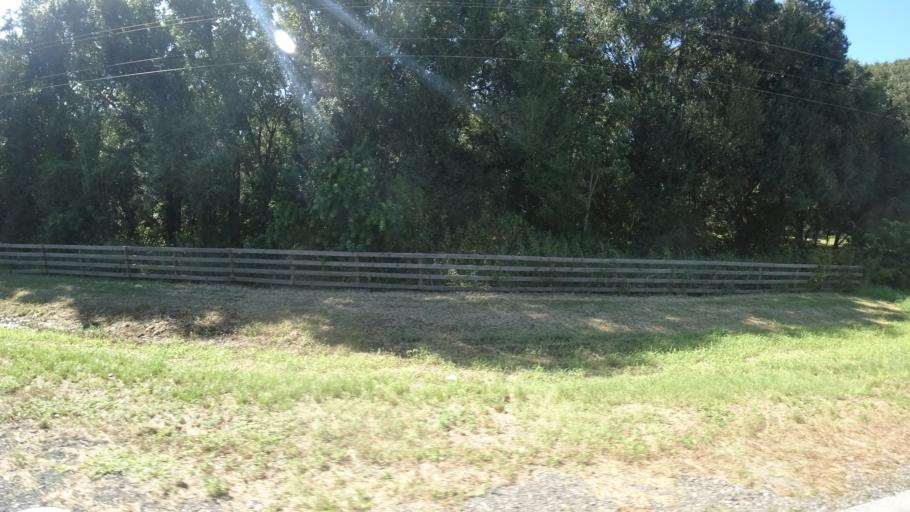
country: US
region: Florida
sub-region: Sarasota County
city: The Meadows
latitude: 27.4598
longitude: -82.3033
